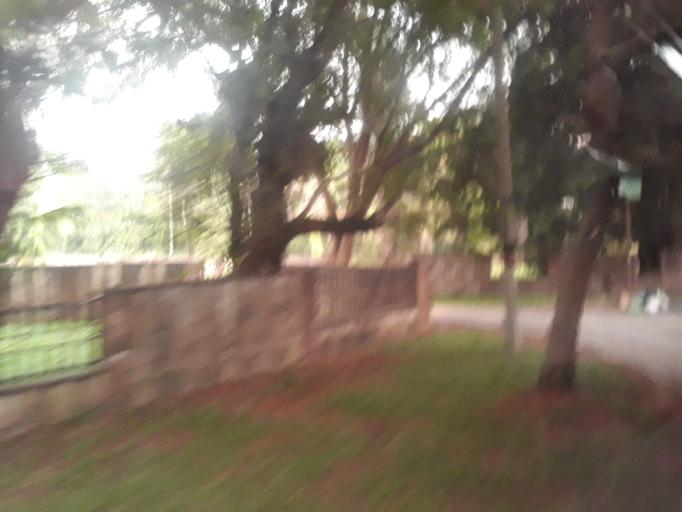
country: MY
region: Perak
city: Ipoh
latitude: 4.5981
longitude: 101.1071
